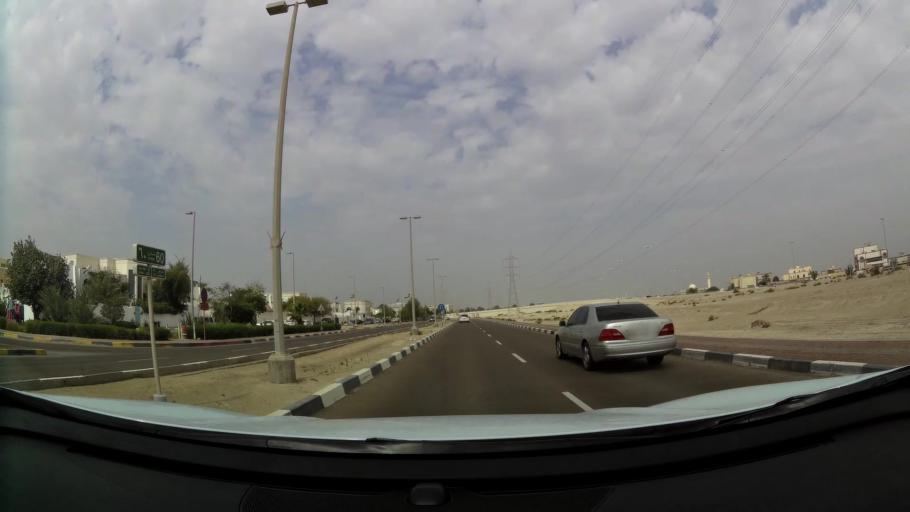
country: AE
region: Abu Dhabi
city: Abu Dhabi
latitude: 24.3227
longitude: 54.6260
